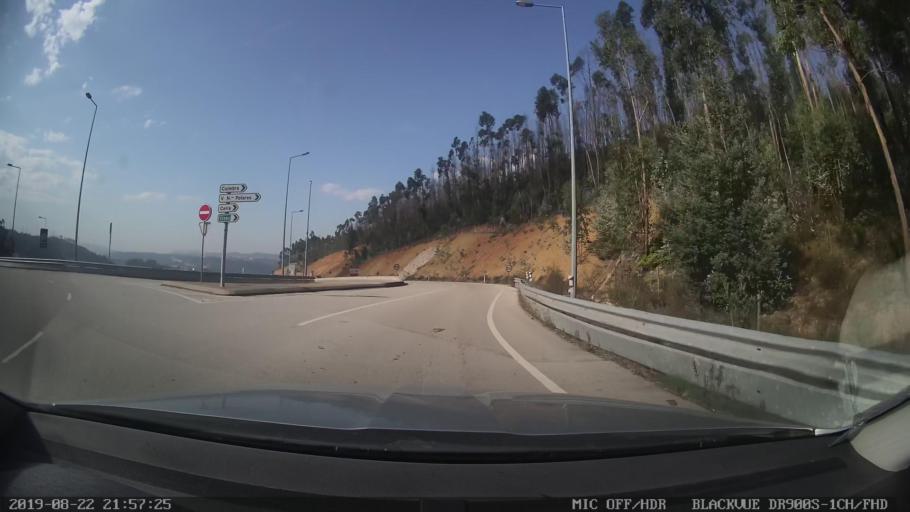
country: PT
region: Coimbra
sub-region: Coimbra
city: Coimbra
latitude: 40.1832
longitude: -8.3799
